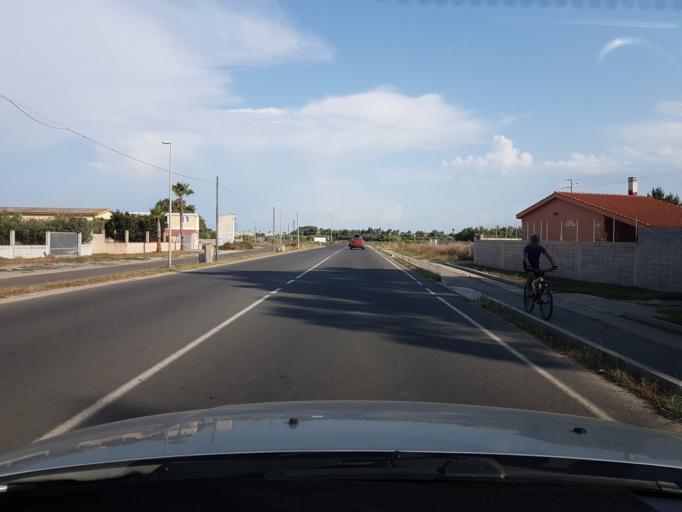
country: IT
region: Sardinia
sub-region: Provincia di Oristano
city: Cabras
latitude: 39.9157
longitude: 8.5406
